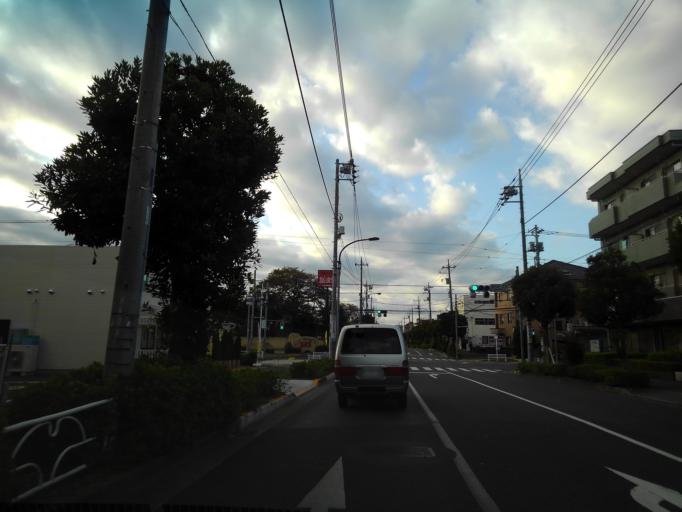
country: JP
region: Tokyo
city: Kokubunji
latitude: 35.7232
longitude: 139.4976
